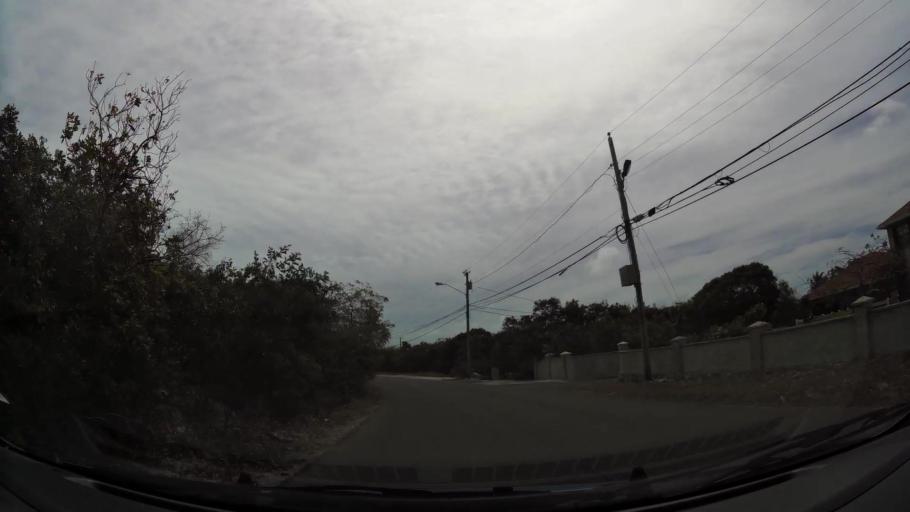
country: BS
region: Mayaguana
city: Abraham's Bay
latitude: 21.7844
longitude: -72.2459
